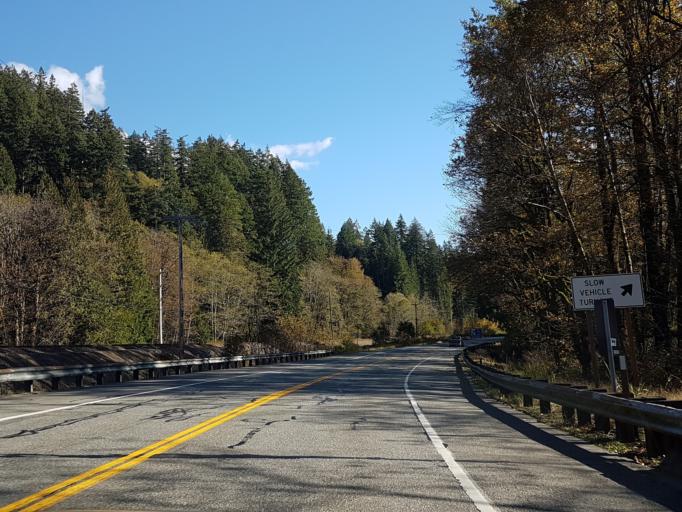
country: US
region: Washington
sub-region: Snohomish County
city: Gold Bar
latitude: 47.7856
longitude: -121.4994
